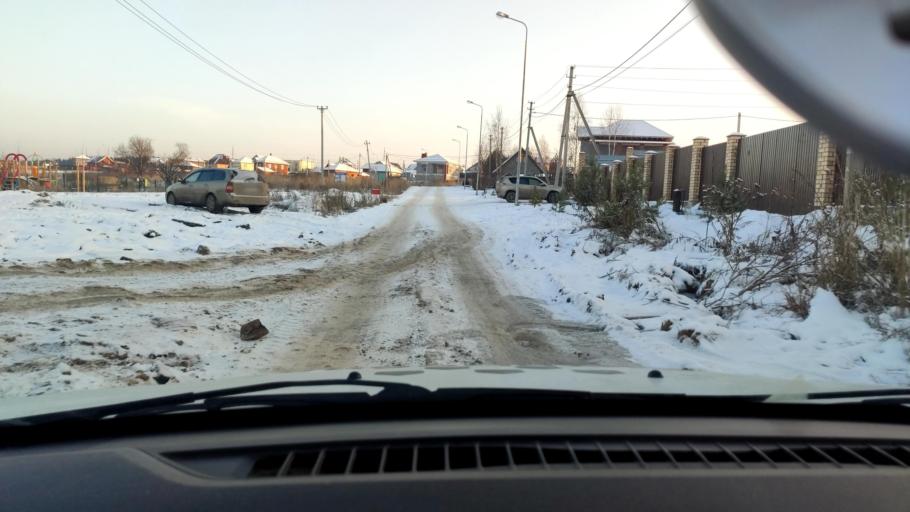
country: RU
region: Perm
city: Perm
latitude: 58.0280
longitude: 56.3499
